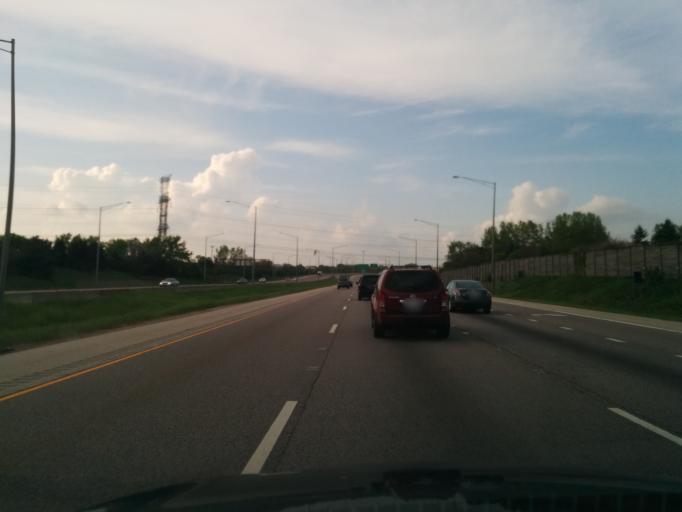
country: US
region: Illinois
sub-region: DuPage County
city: Itasca
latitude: 41.9421
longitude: -88.0374
